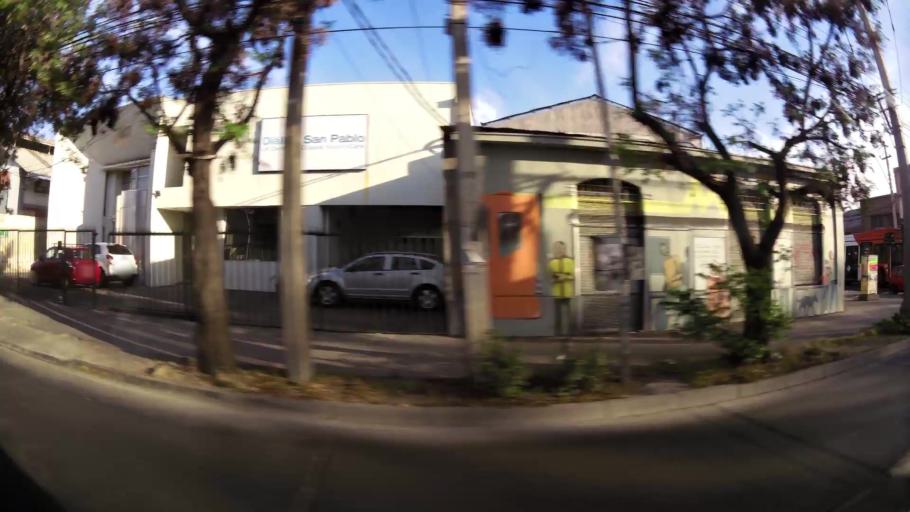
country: CL
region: Santiago Metropolitan
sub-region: Provincia de Santiago
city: Lo Prado
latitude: -33.4388
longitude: -70.6959
